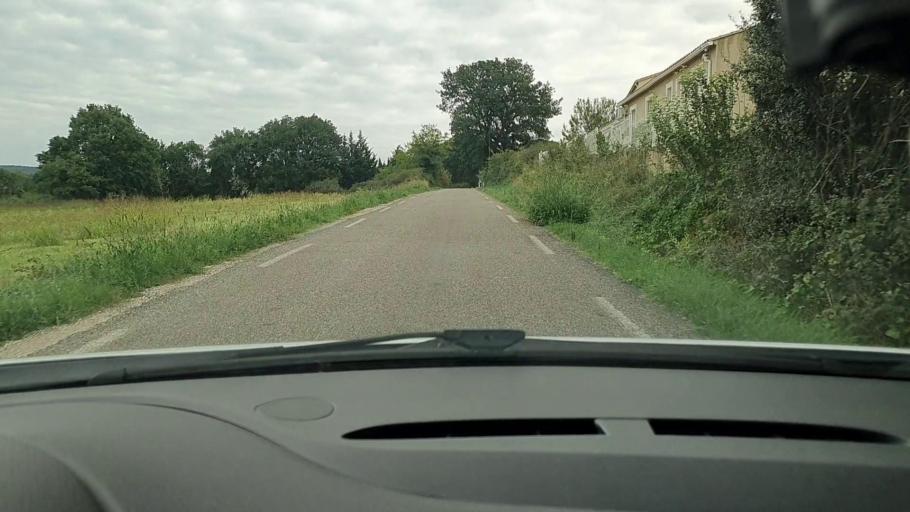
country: FR
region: Languedoc-Roussillon
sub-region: Departement du Gard
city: Saint-Chaptes
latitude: 44.0370
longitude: 4.2948
